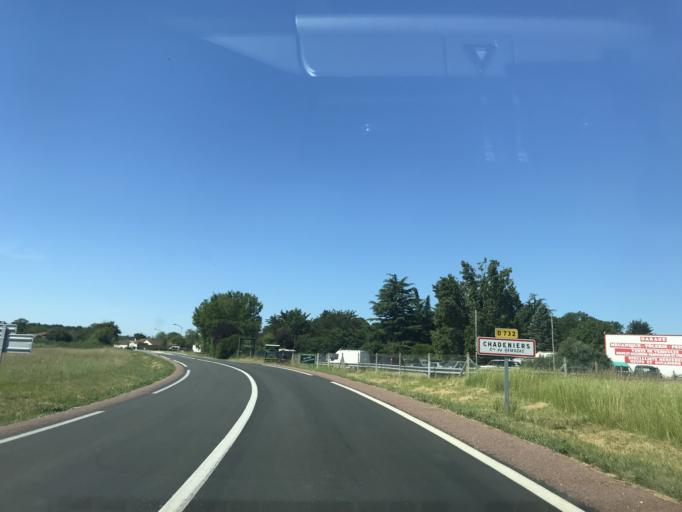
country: FR
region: Poitou-Charentes
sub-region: Departement de la Charente-Maritime
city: Gemozac
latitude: 45.5680
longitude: -0.7171
